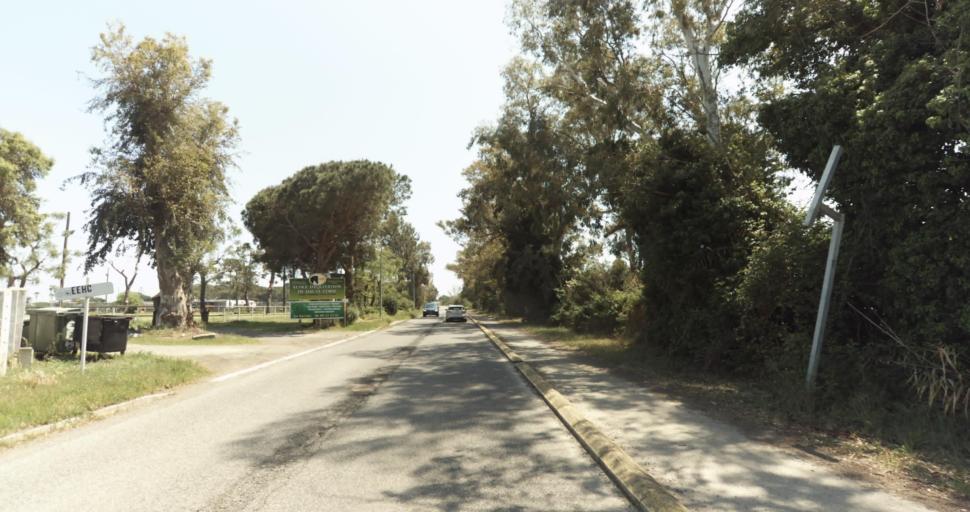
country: FR
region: Corsica
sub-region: Departement de la Haute-Corse
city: Biguglia
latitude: 42.6465
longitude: 9.4542
